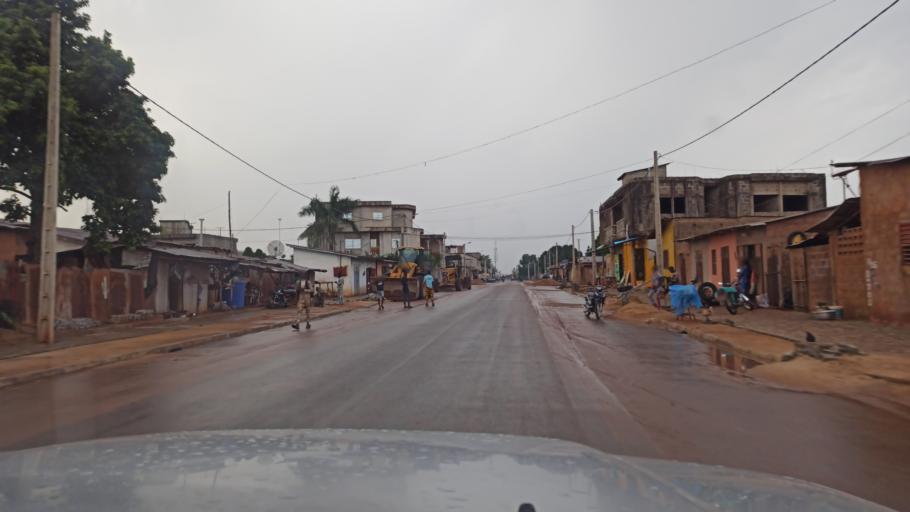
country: BJ
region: Queme
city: Porto-Novo
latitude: 6.4940
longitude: 2.6453
